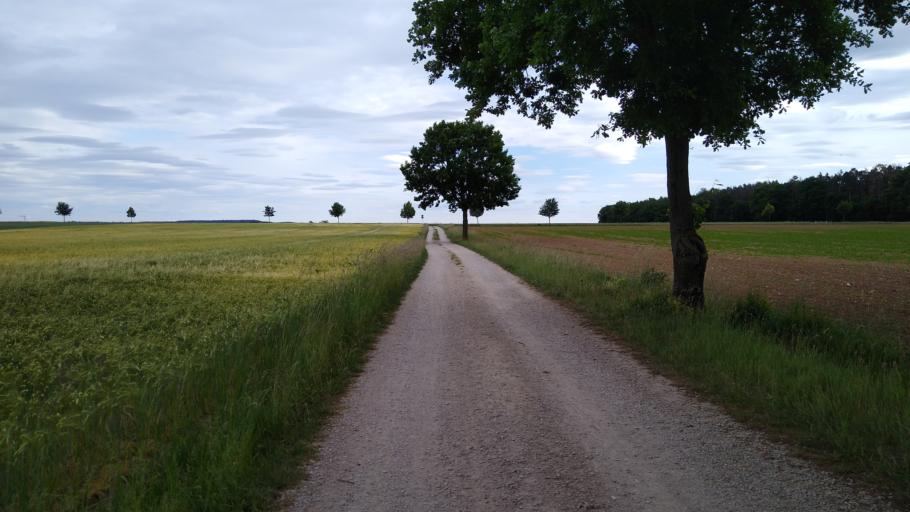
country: DE
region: Bavaria
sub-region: Regierungsbezirk Mittelfranken
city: Obermichelbach
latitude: 49.5309
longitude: 10.8945
